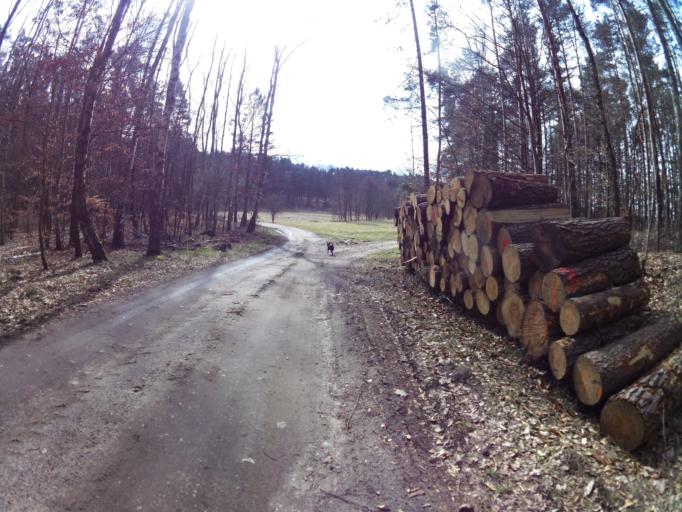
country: PL
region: West Pomeranian Voivodeship
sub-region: Powiat mysliborski
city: Mysliborz
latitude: 52.8537
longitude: 14.8405
